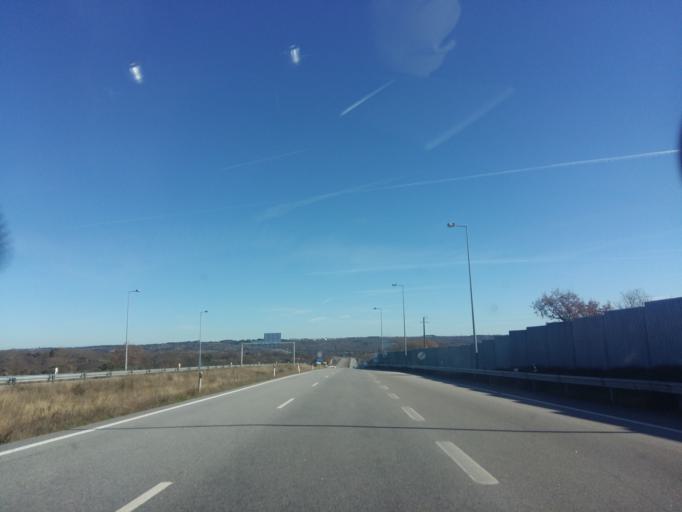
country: PT
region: Guarda
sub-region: Guarda
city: Sequeira
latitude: 40.6045
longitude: -7.0644
